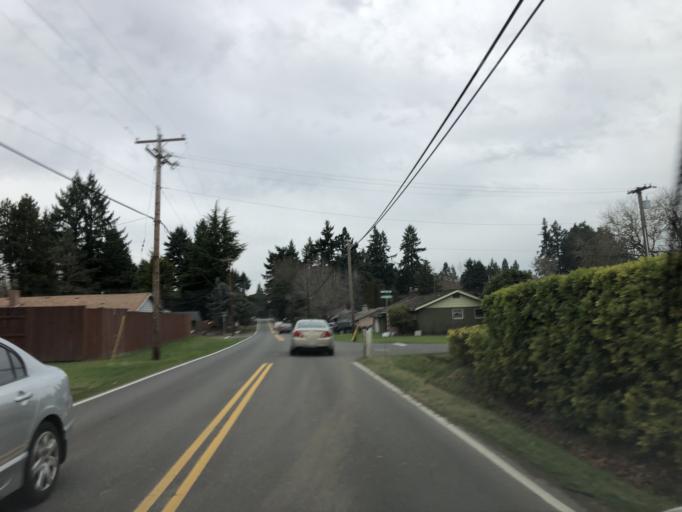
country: US
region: Oregon
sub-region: Washington County
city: King City
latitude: 45.4255
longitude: -122.7998
